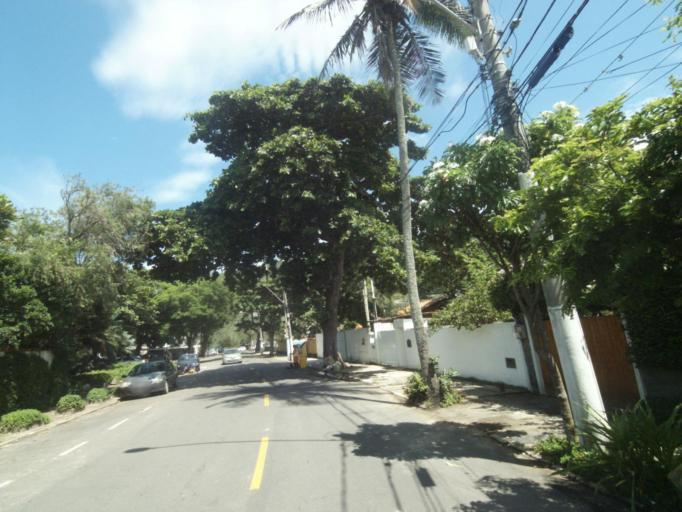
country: BR
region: Rio de Janeiro
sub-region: Niteroi
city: Niteroi
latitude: -22.9735
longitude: -43.0371
